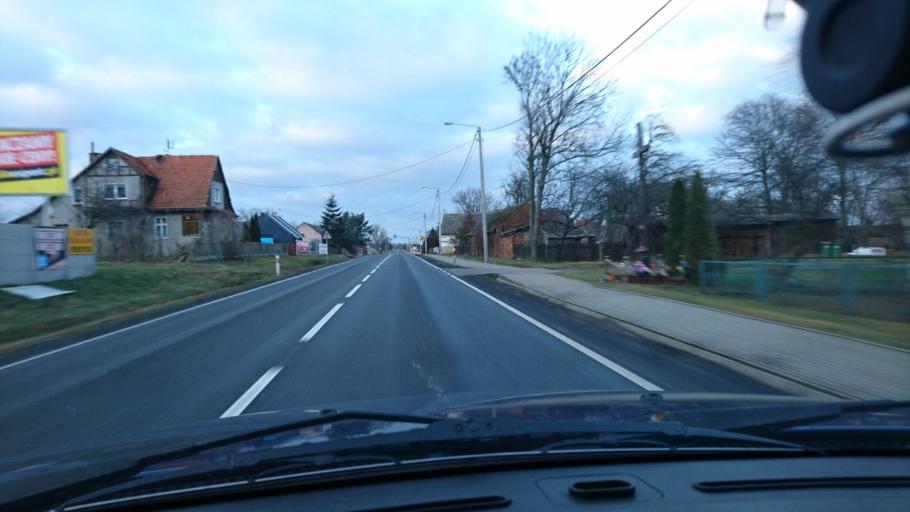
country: PL
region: Greater Poland Voivodeship
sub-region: Powiat ostrzeszowski
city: Ostrzeszow
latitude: 51.3530
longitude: 17.9474
